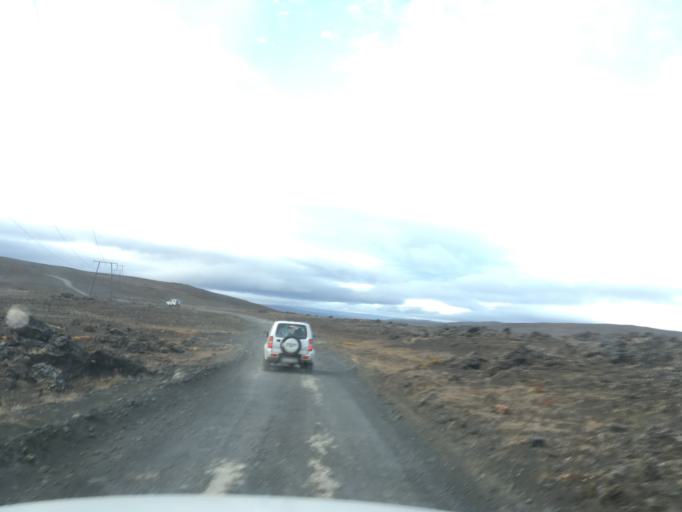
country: IS
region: South
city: Vestmannaeyjar
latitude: 64.1517
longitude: -19.1356
